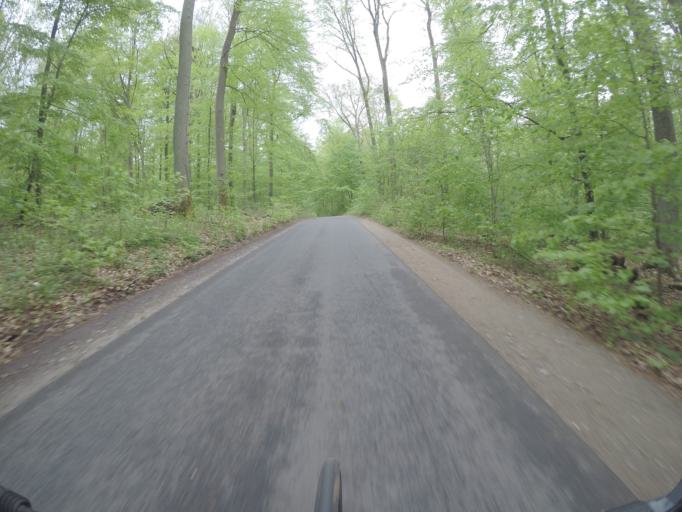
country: DE
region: Brandenburg
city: Marienwerder
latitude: 52.8960
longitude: 13.6506
